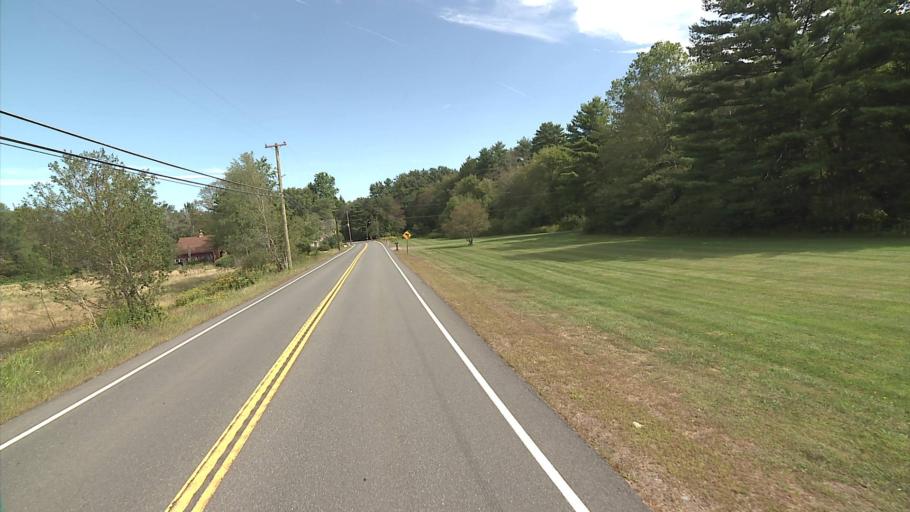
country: US
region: Connecticut
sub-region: Tolland County
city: Stafford
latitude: 42.0111
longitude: -72.3169
